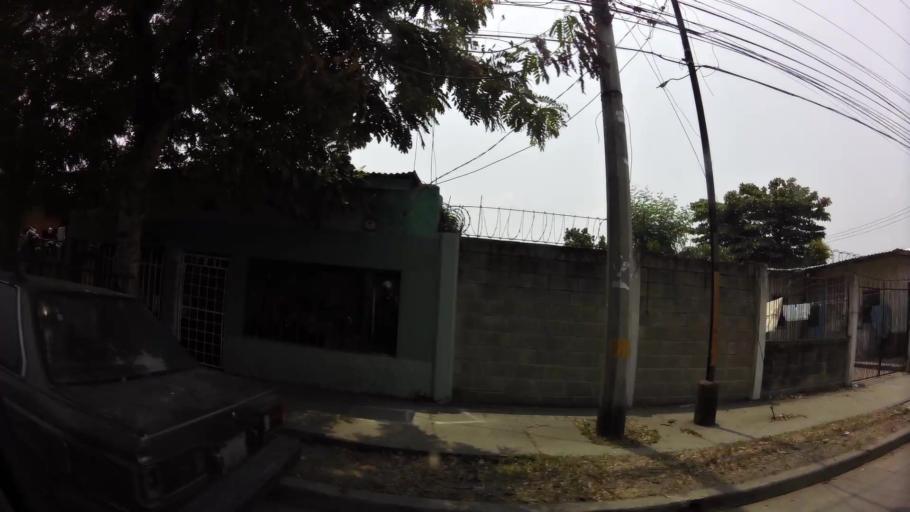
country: HN
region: Cortes
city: San Pedro Sula
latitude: 15.4952
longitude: -88.0107
